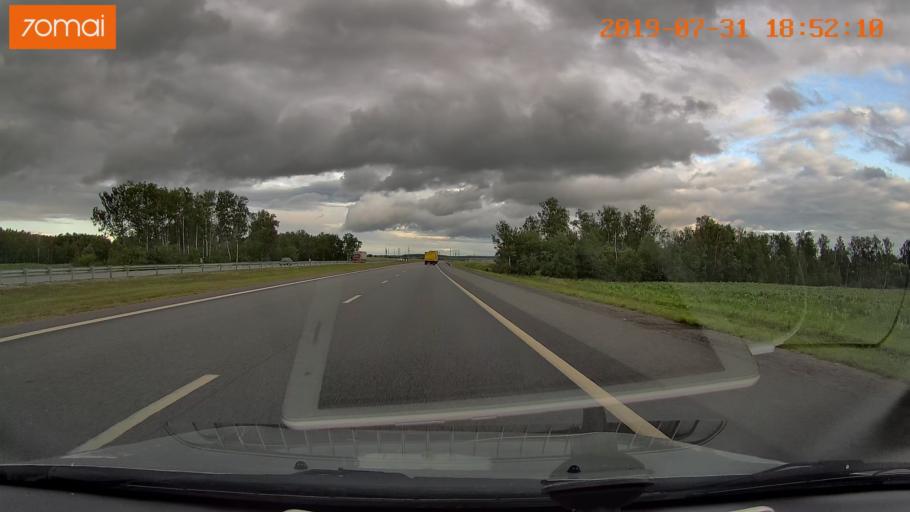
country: RU
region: Moskovskaya
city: Voskresensk
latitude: 55.2163
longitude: 38.6251
